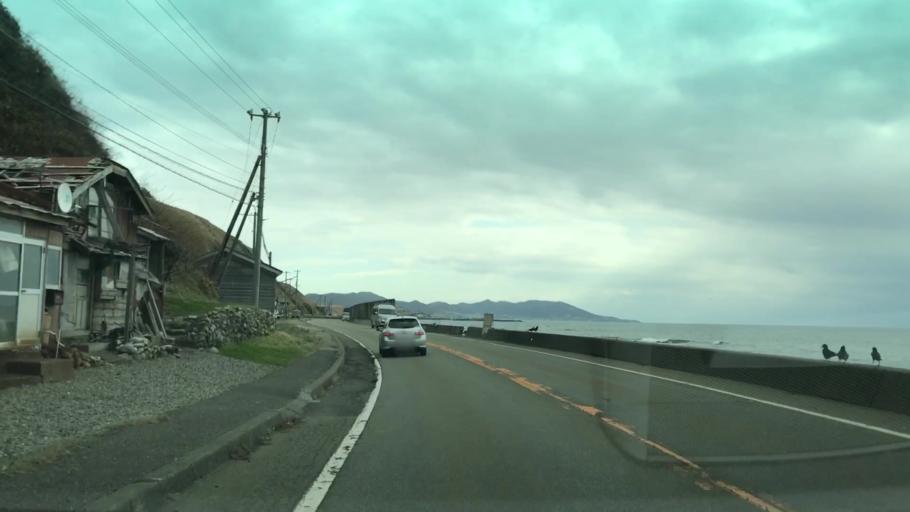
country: JP
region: Hokkaido
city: Shizunai-furukawacho
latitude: 42.0545
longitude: 143.0839
